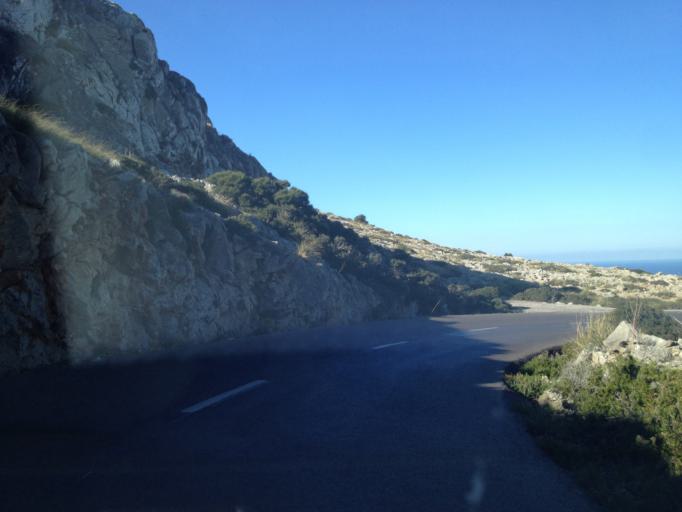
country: ES
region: Balearic Islands
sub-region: Illes Balears
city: Alcudia
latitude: 39.9572
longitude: 3.2077
